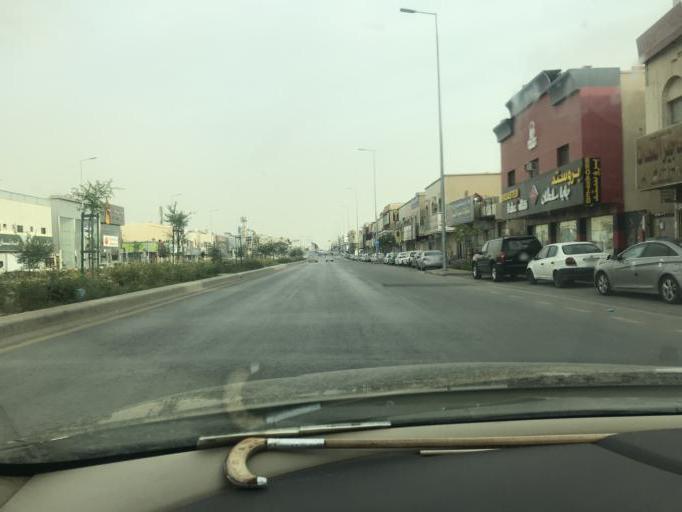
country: SA
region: Ar Riyad
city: Riyadh
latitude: 24.7427
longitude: 46.7776
